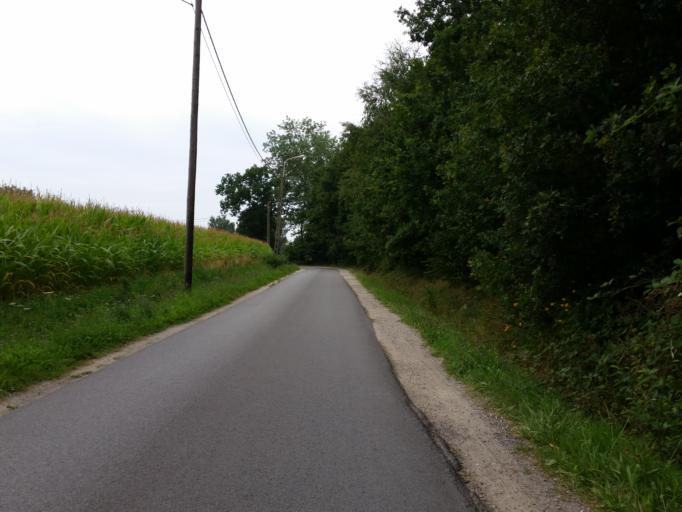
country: BE
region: Flanders
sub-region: Provincie Vlaams-Brabant
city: Zemst
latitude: 50.9887
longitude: 4.4410
